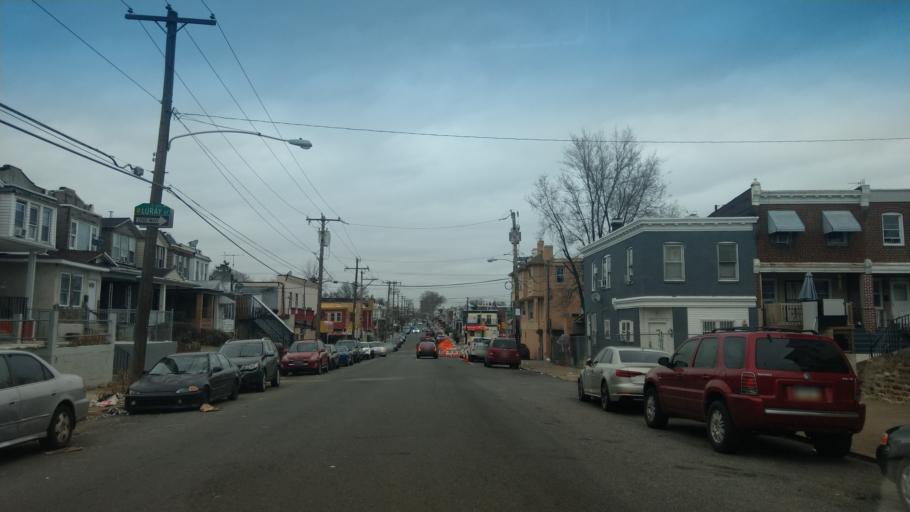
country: US
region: Pennsylvania
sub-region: Montgomery County
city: Rockledge
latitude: 40.0197
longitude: -75.1163
